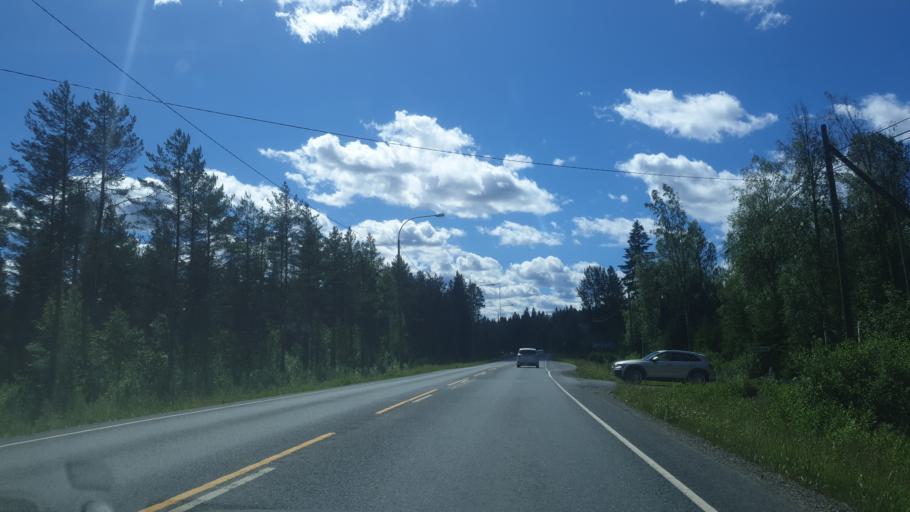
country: FI
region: Northern Savo
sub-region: Varkaus
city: Leppaevirta
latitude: 62.5607
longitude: 27.6211
